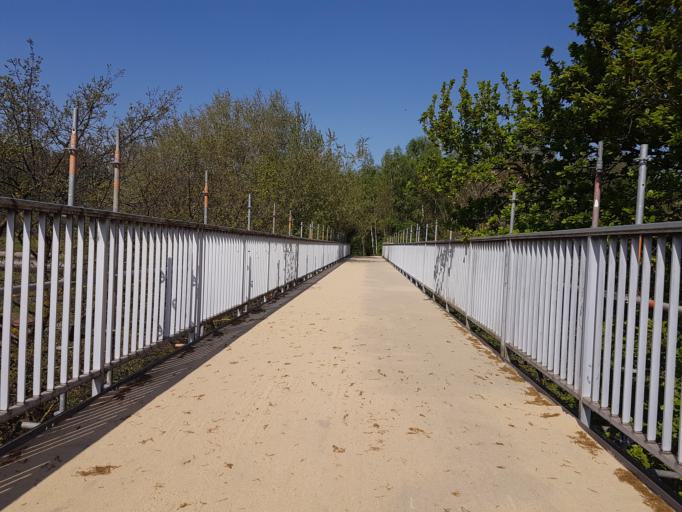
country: DE
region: North Rhine-Westphalia
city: Witten
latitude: 51.4321
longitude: 7.3156
